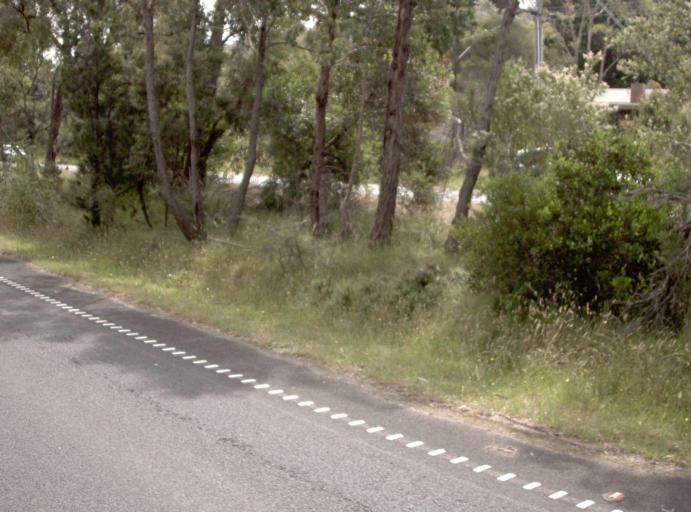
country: AU
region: Victoria
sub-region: Mornington Peninsula
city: Moorooduc
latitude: -38.2013
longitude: 145.1266
